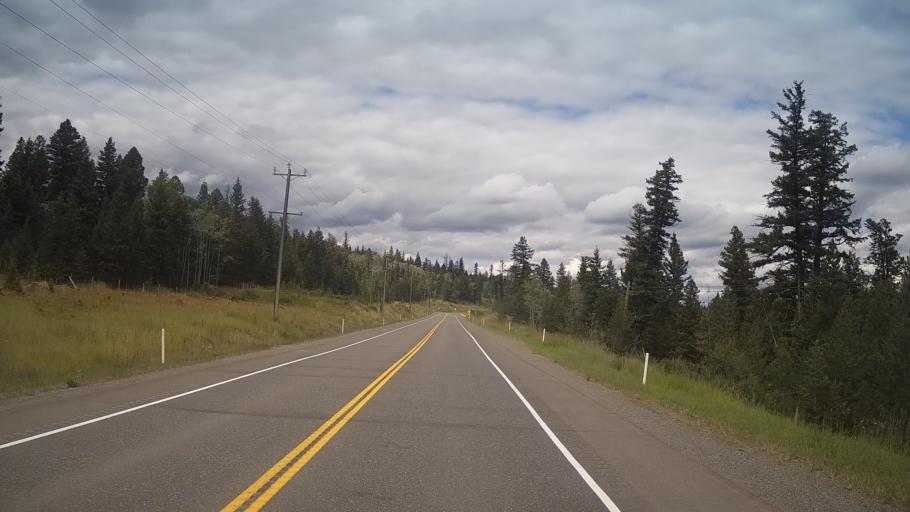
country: CA
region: British Columbia
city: Cache Creek
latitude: 51.1829
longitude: -121.5153
